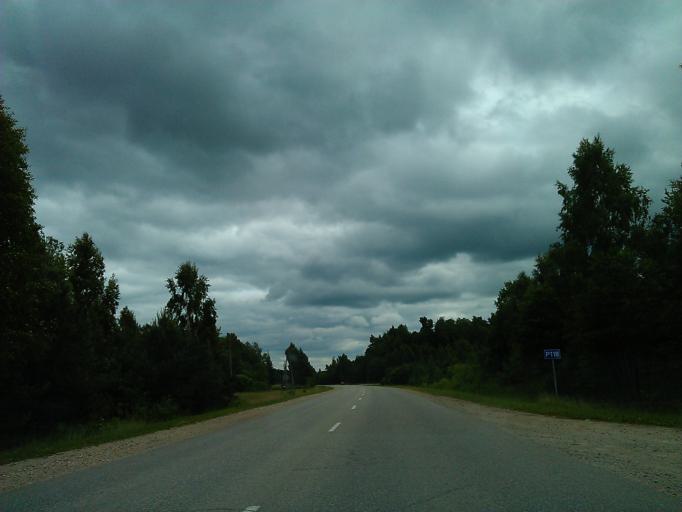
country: LV
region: Kuldigas Rajons
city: Kuldiga
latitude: 56.9646
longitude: 21.9369
